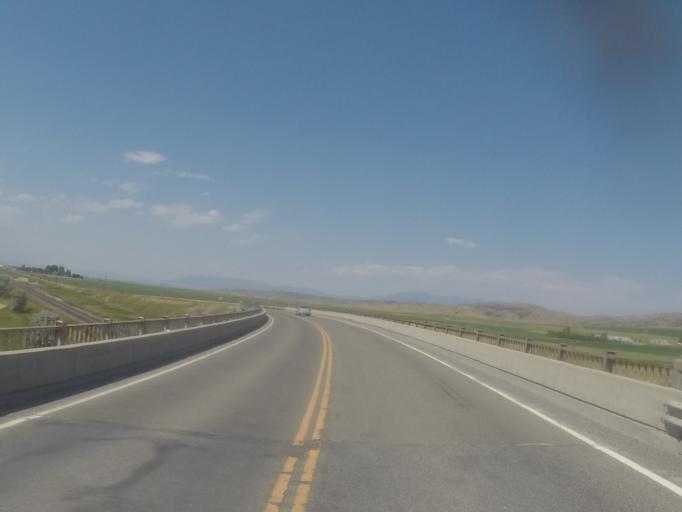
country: US
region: Montana
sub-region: Broadwater County
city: Townsend
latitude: 46.1768
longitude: -111.4440
